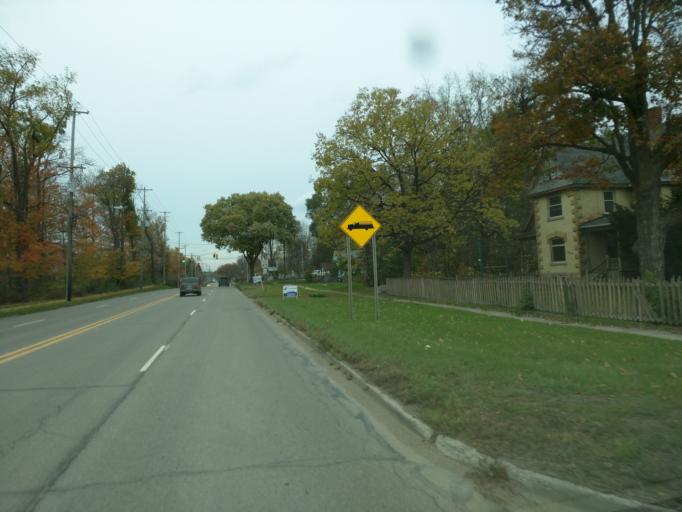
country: US
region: Michigan
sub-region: Ingham County
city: Lansing
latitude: 42.7558
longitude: -84.5598
